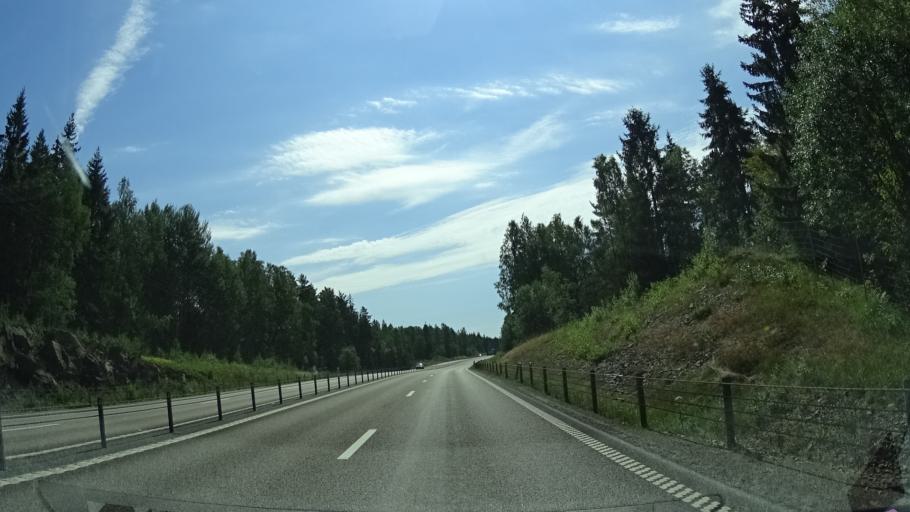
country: SE
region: Vaermland
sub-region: Kristinehamns Kommun
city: Kristinehamn
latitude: 59.3440
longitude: 14.0864
